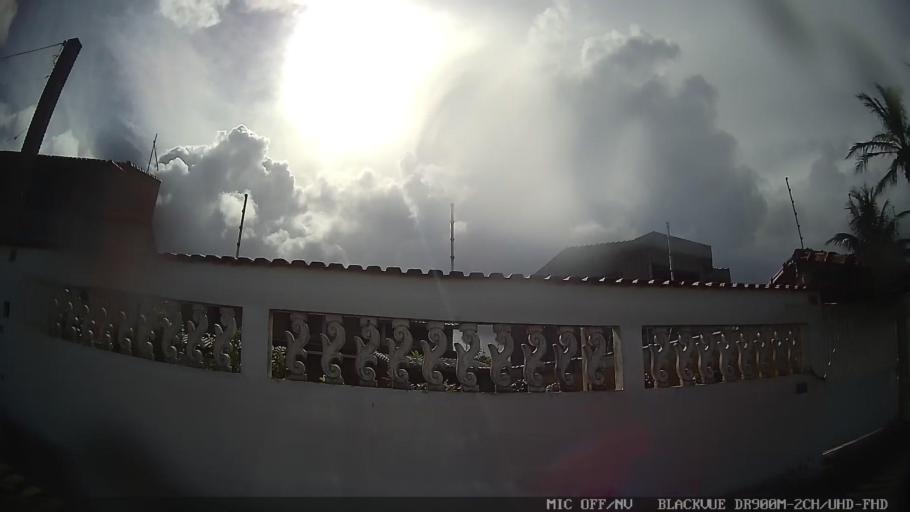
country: BR
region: Sao Paulo
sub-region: Itanhaem
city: Itanhaem
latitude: -24.2389
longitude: -46.8752
